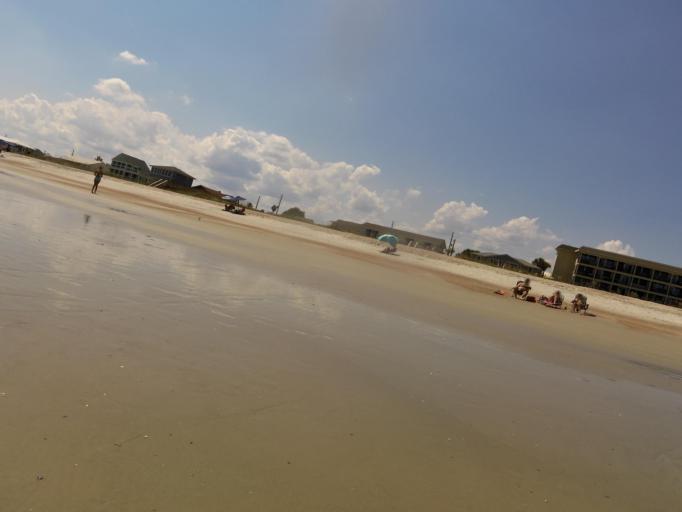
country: US
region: Florida
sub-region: Nassau County
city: Fernandina Beach
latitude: 30.6609
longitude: -81.4308
